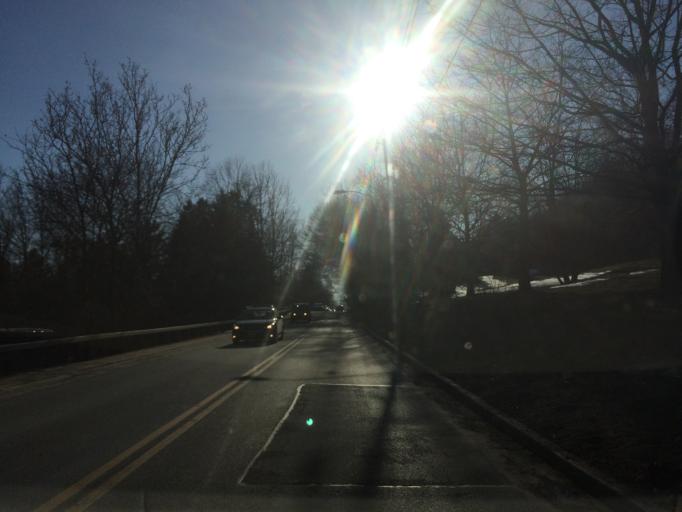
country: US
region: New York
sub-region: Monroe County
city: Brighton
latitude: 43.1345
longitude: -77.5808
